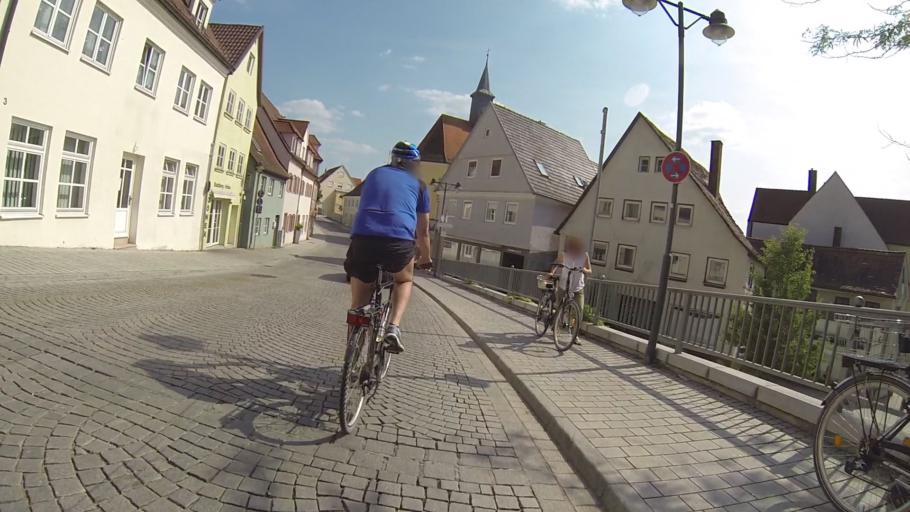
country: DE
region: Bavaria
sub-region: Swabia
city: Guenzburg
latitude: 48.4545
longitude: 10.2745
